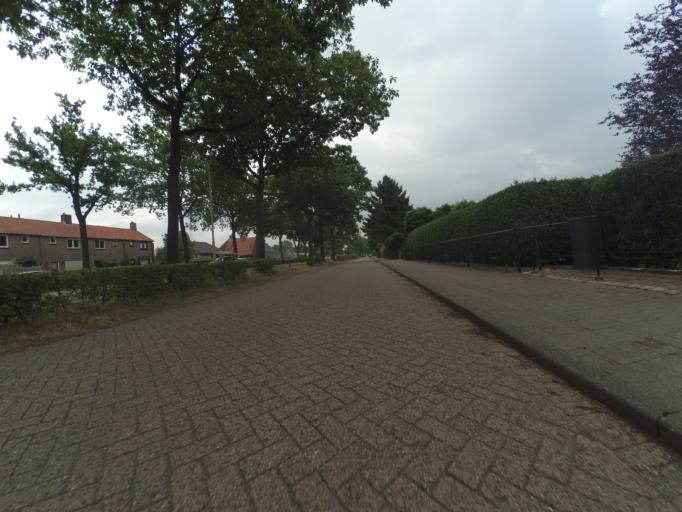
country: NL
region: North Brabant
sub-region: Gemeente Woensdrecht
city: Woensdrecht
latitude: 51.4183
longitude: 4.3318
